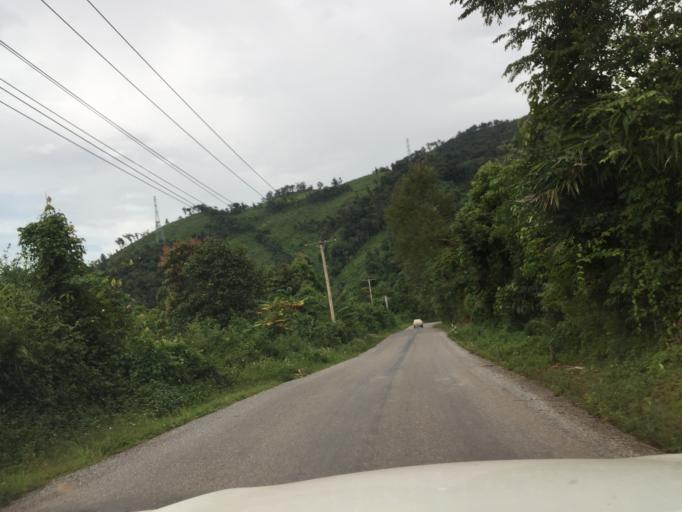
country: LA
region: Phongsali
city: Phongsali
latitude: 21.3428
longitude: 102.0504
